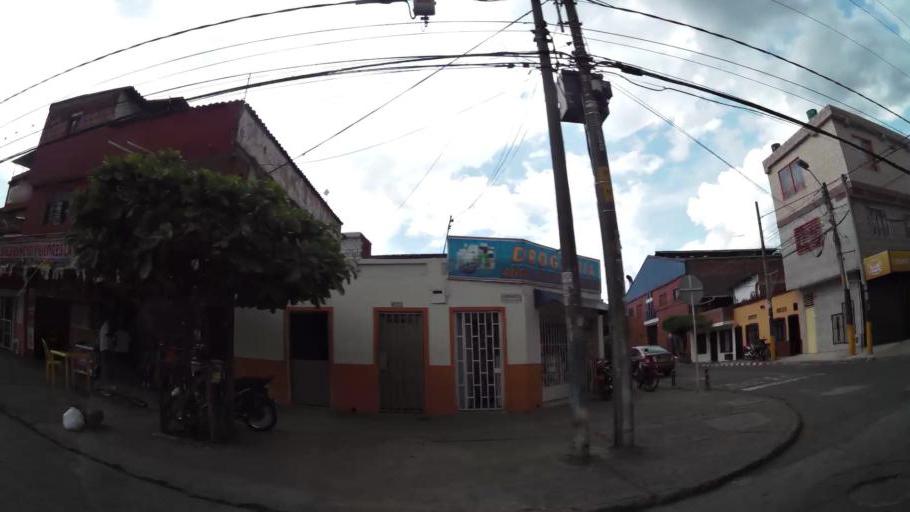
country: CO
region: Valle del Cauca
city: Cali
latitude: 3.4765
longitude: -76.5079
